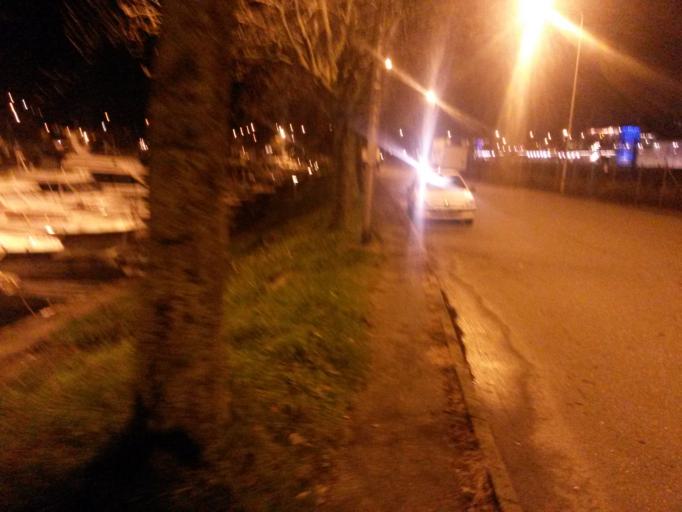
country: NO
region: Rogaland
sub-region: Stavanger
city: Stavanger
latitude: 58.9584
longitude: 5.7424
